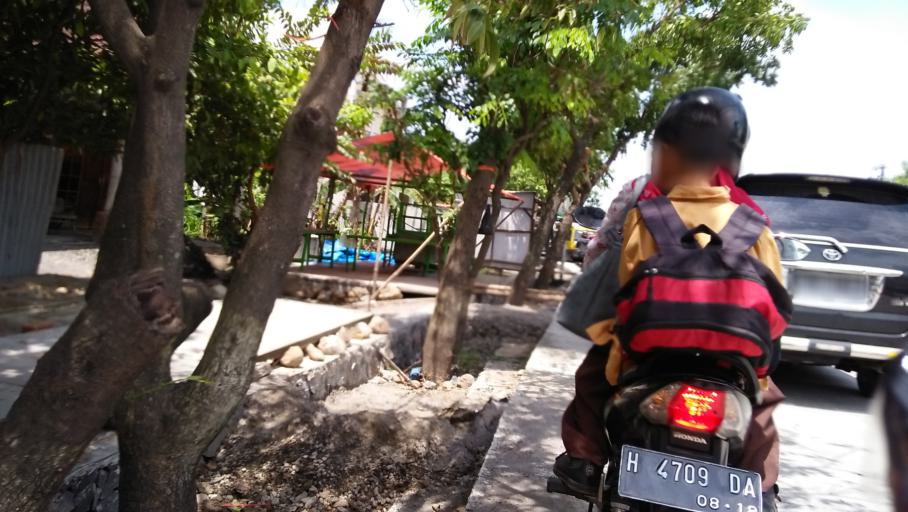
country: ID
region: Central Java
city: Mranggen
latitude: -6.9726
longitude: 110.4816
